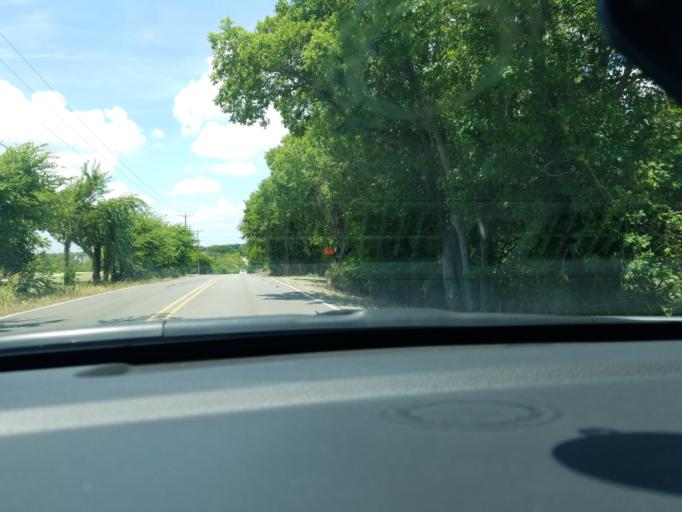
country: US
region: Texas
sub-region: Dallas County
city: Sunnyvale
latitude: 32.8139
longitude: -96.5738
